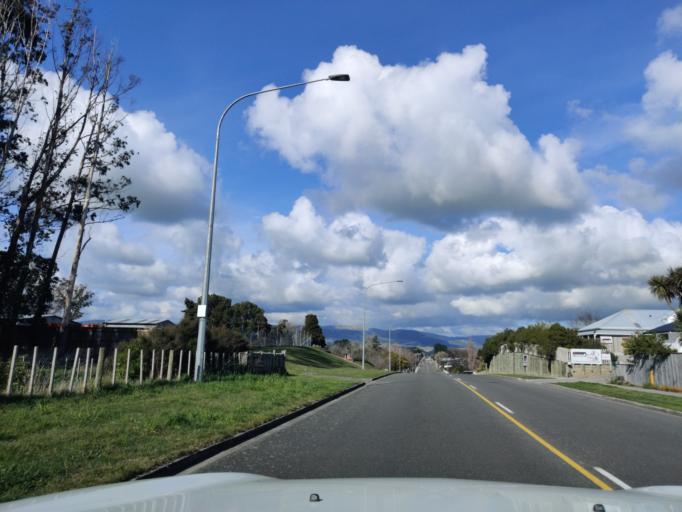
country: NZ
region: Manawatu-Wanganui
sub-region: Palmerston North City
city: Palmerston North
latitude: -40.3224
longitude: 175.6597
